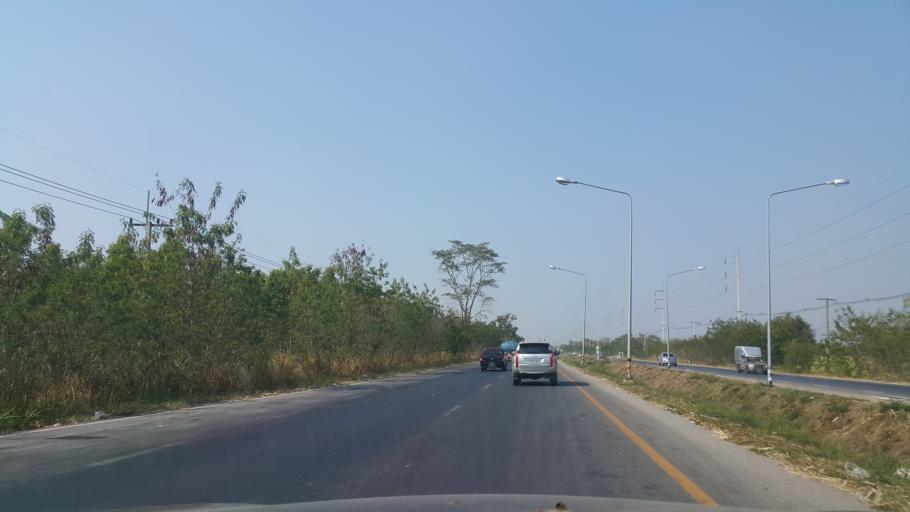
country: TH
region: Chaiyaphum
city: Phu Khiao
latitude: 16.4390
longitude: 102.1262
